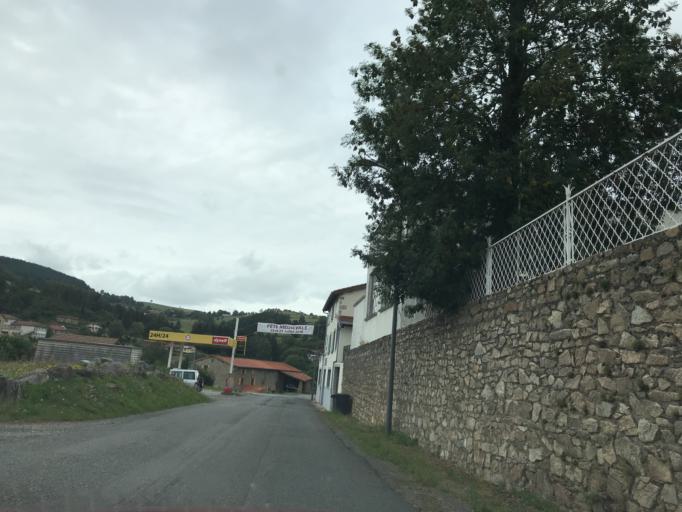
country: FR
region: Rhone-Alpes
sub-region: Departement de la Loire
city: Sail-sous-Couzan
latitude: 45.7022
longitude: 3.8543
